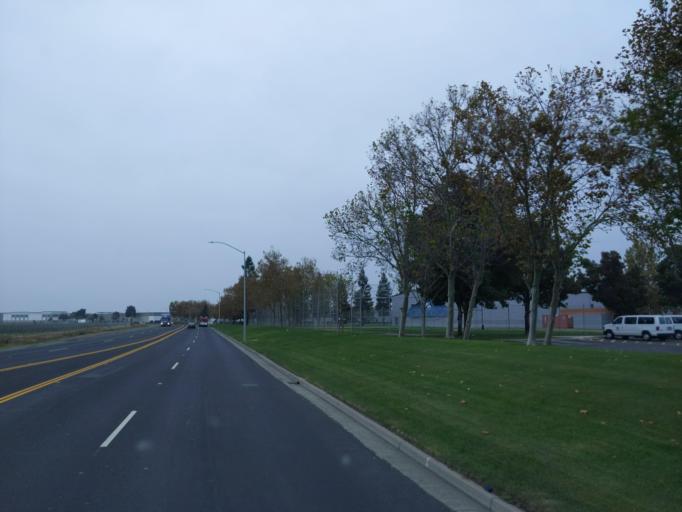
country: US
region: California
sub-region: San Joaquin County
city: Kennedy
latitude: 37.9055
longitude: -121.2304
